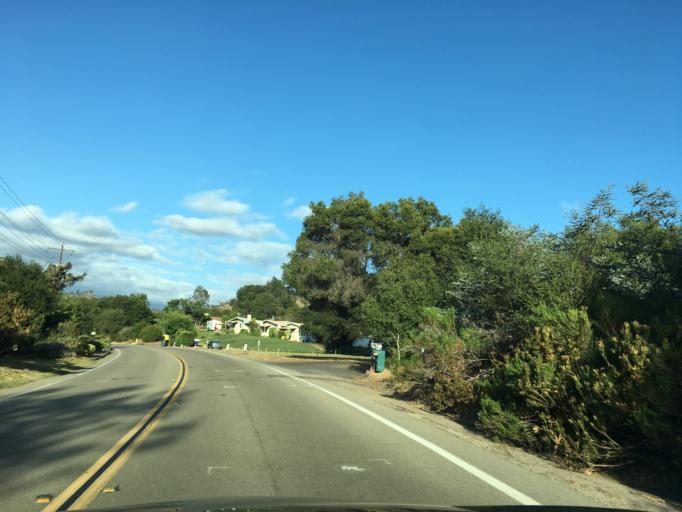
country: US
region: California
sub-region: San Diego County
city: Hidden Meadows
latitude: 33.2496
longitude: -117.1393
